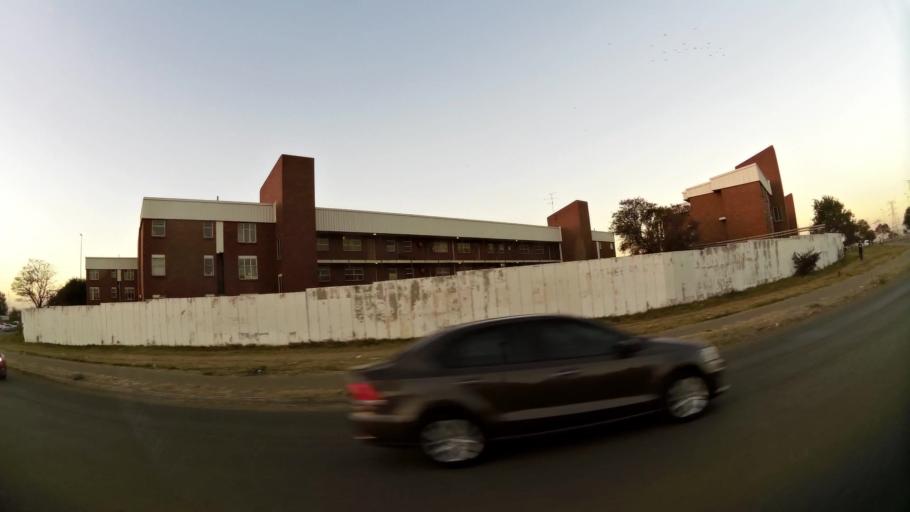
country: ZA
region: North-West
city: Ga-Rankuwa
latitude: -25.6202
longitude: 28.0068
